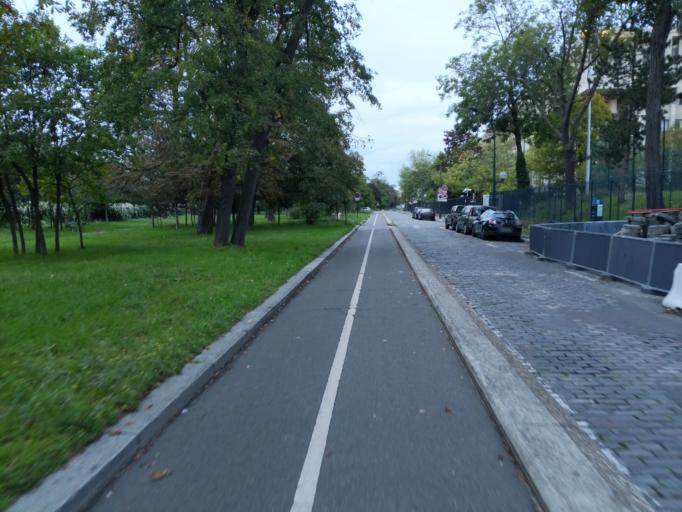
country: FR
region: Ile-de-France
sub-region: Departement des Hauts-de-Seine
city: Neuilly-sur-Seine
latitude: 48.8655
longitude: 2.2688
